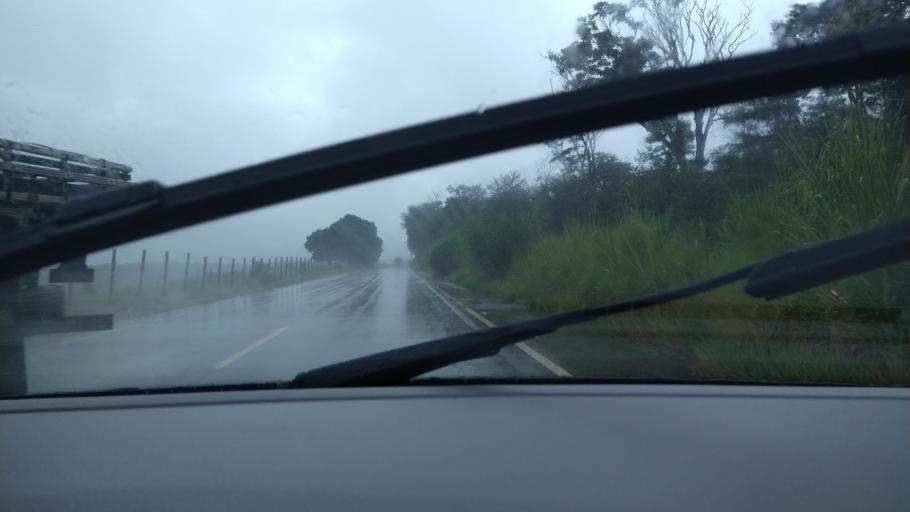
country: BR
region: Minas Gerais
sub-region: Ponte Nova
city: Ponte Nova
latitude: -20.5500
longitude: -42.8823
